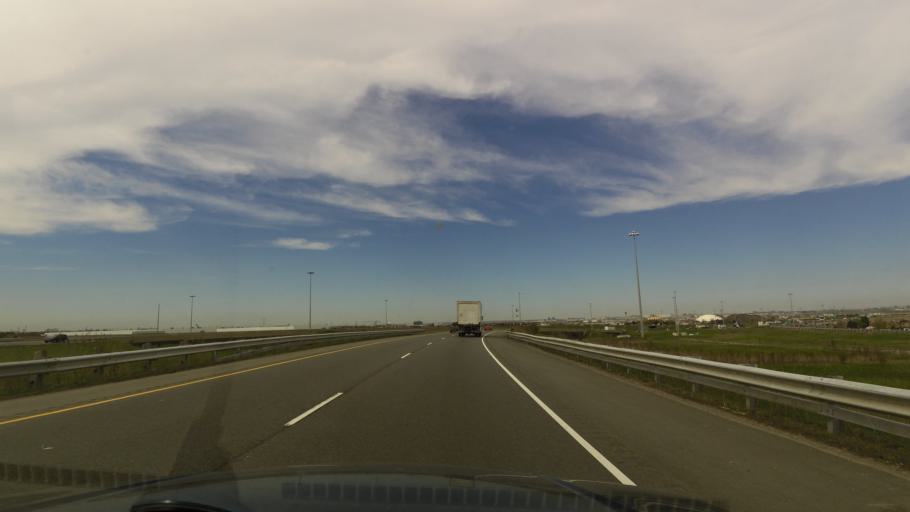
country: CA
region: Ontario
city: Mississauga
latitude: 43.6385
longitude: -79.6547
